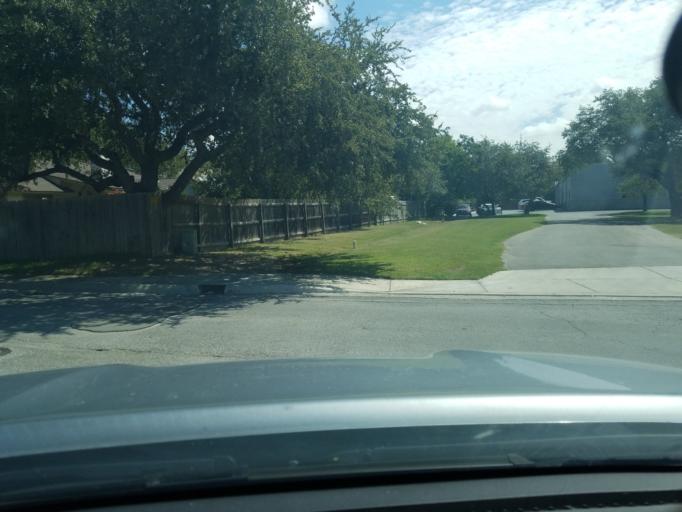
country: US
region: Texas
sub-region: Bexar County
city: Shavano Park
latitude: 29.5637
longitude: -98.6111
